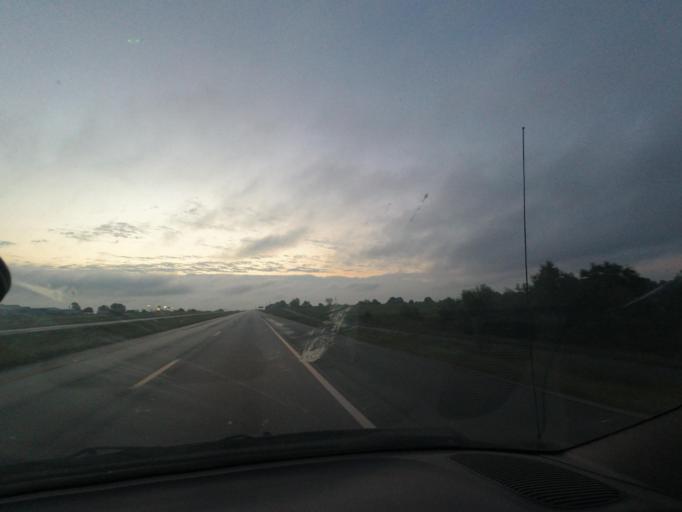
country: US
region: Missouri
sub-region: Linn County
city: Brookfield
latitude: 39.7625
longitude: -93.0141
